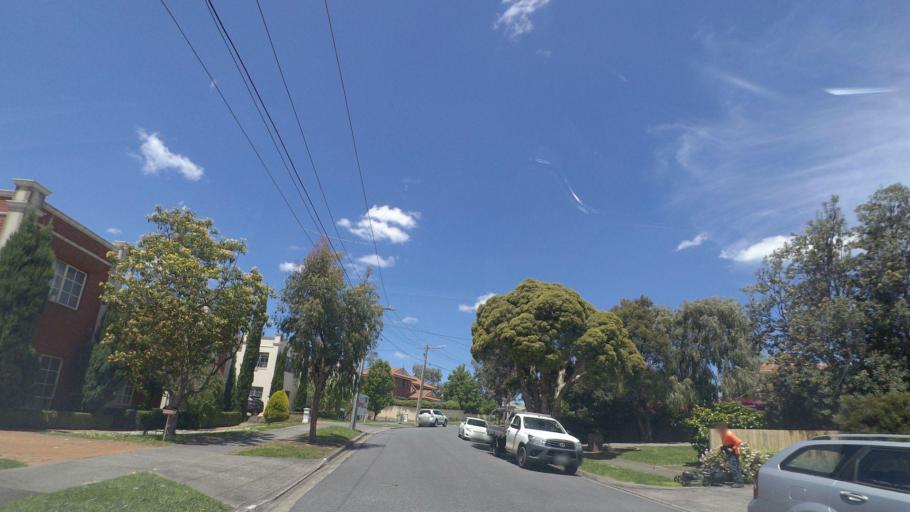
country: AU
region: Victoria
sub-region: Knox
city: Wantirna
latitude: -37.8360
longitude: 145.2108
